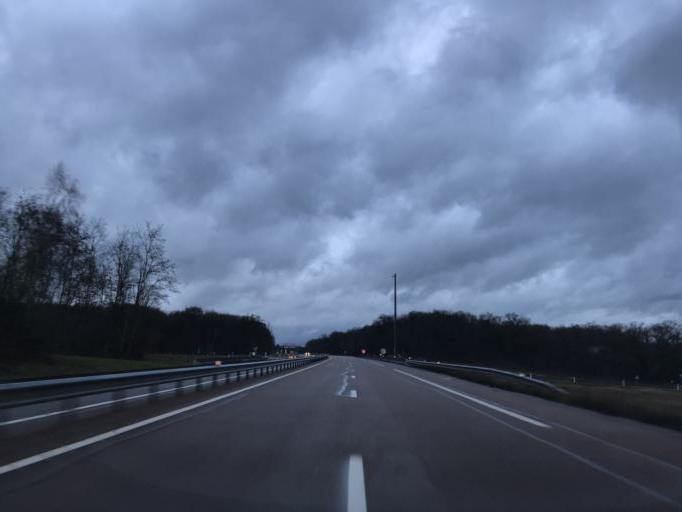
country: FR
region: Franche-Comte
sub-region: Departement du Jura
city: Choisey
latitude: 47.0661
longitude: 5.4382
